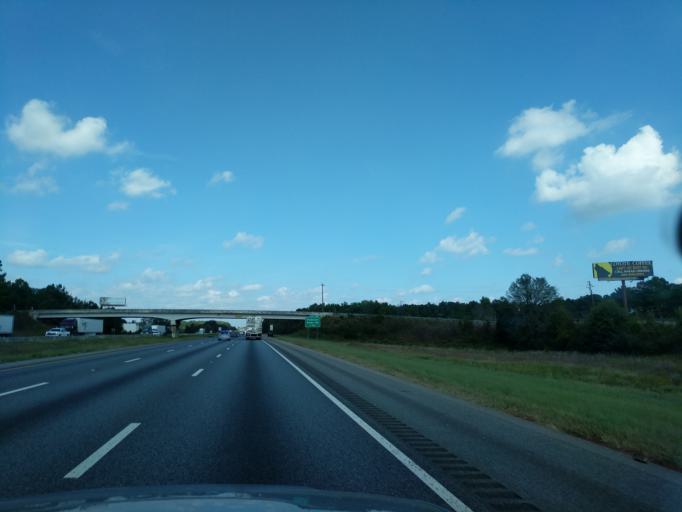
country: US
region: South Carolina
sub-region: Greenville County
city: Golden Grove
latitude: 34.7393
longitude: -82.4850
